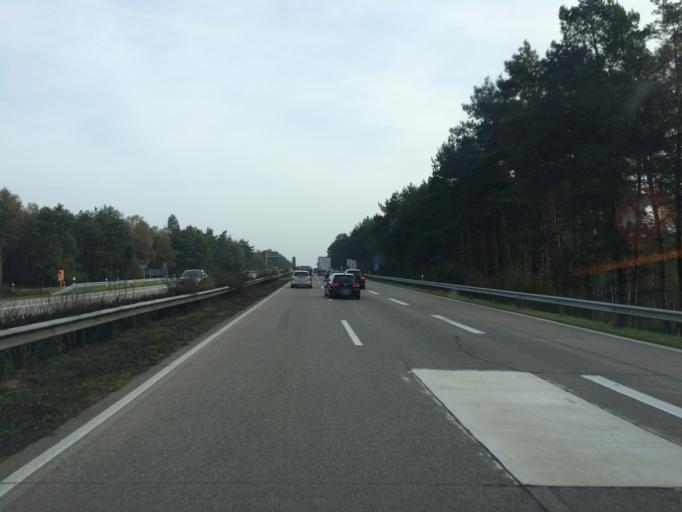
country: DE
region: Lower Saxony
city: Soltau
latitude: 52.9457
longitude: 9.8723
